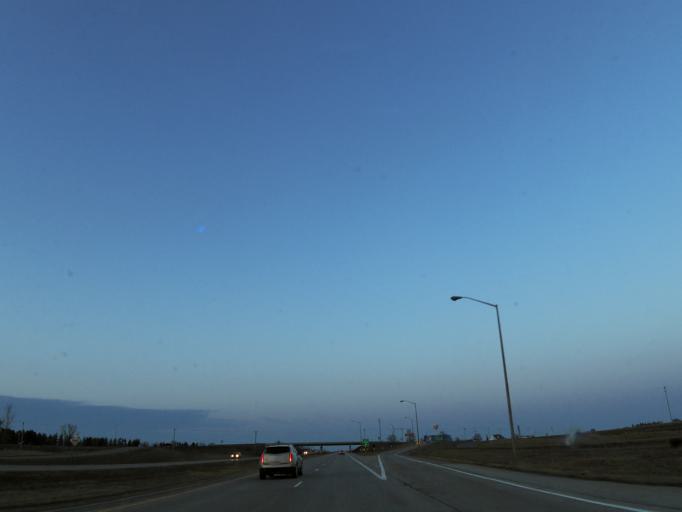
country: US
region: Minnesota
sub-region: Mower County
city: Grand Meadow
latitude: 43.7081
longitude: -92.7039
